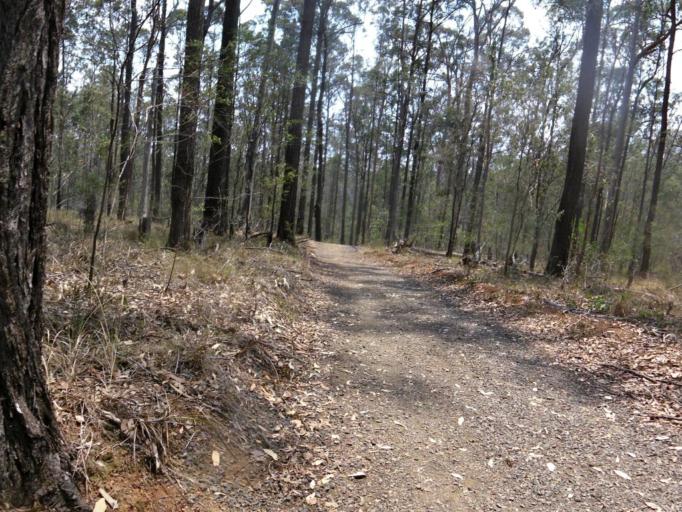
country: AU
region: Queensland
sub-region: Logan
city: Springwood
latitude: -27.6081
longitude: 153.1534
